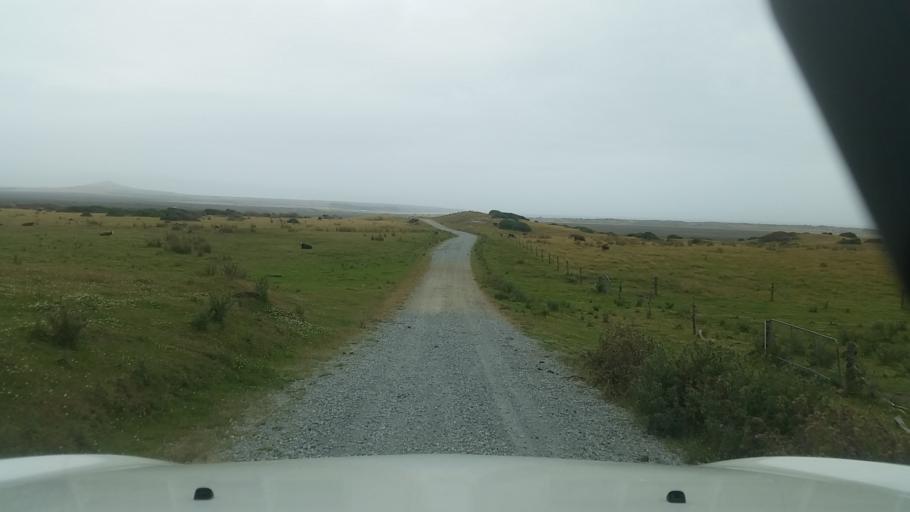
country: NZ
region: Chatham Islands
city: Waitangi
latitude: -43.7747
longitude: -176.7749
